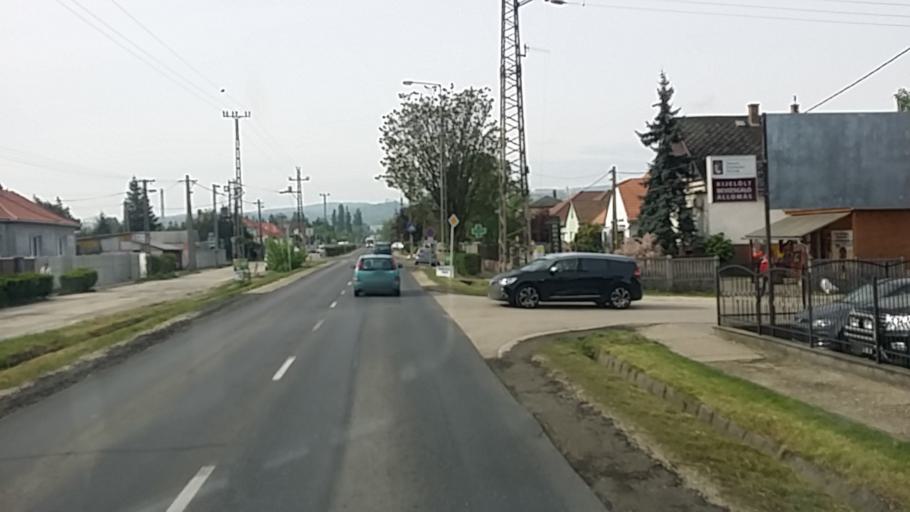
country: HU
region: Komarom-Esztergom
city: Dorog
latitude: 47.7414
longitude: 18.7275
